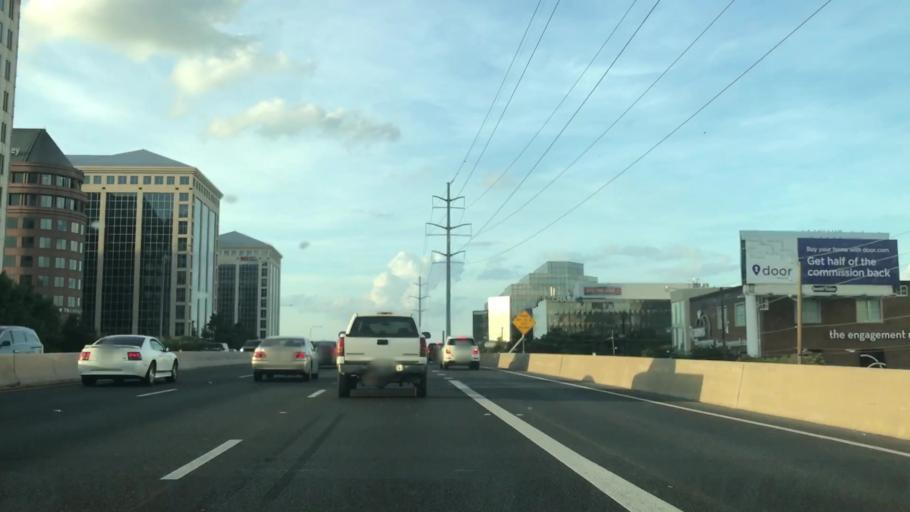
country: US
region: Texas
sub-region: Dallas County
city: Addison
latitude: 32.9384
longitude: -96.8219
